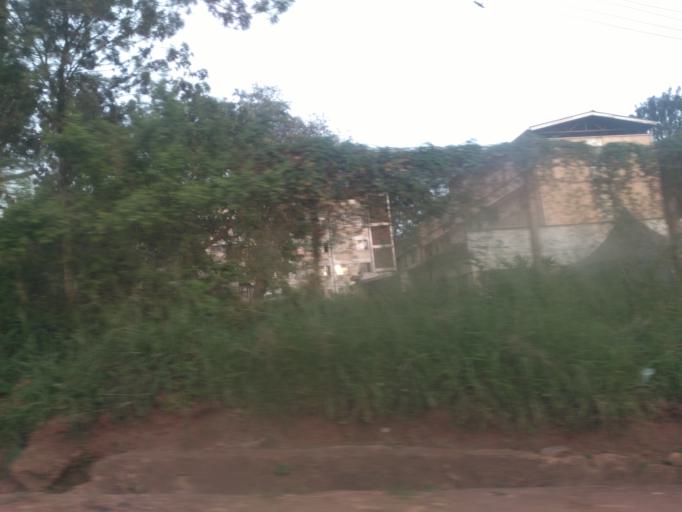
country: UG
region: Central Region
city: Kampala Central Division
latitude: 0.3389
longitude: 32.5774
